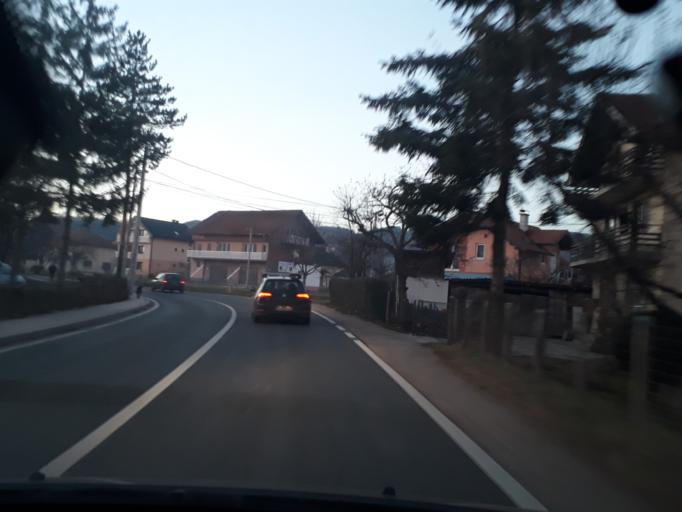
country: BA
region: Federation of Bosnia and Herzegovina
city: Hadzici
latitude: 43.8779
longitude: 18.2056
